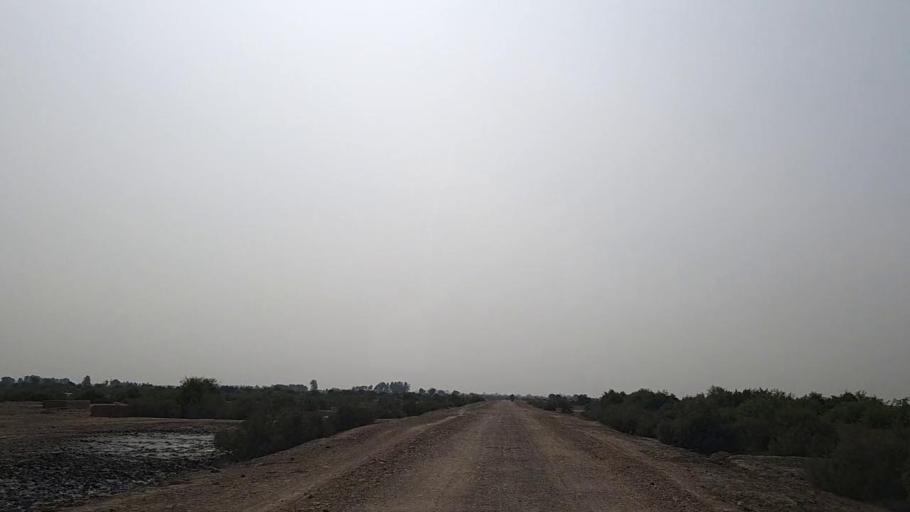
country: PK
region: Sindh
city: Mirpur Sakro
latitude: 24.6416
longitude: 67.7675
